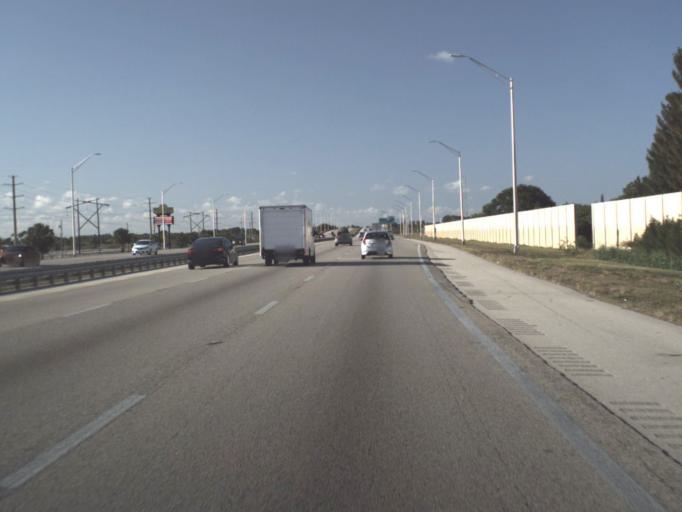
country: US
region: Florida
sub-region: Brevard County
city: June Park
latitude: 28.1124
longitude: -80.7058
